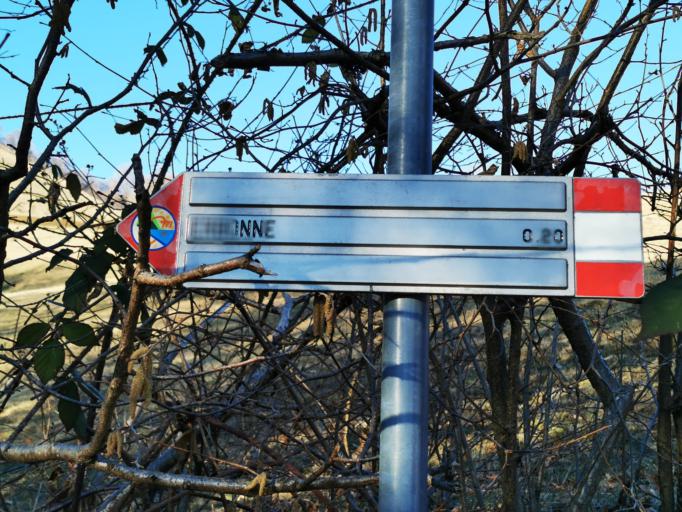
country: IT
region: Lombardy
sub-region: Provincia di Como
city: Casasco Intelvi
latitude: 45.9234
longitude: 9.0639
